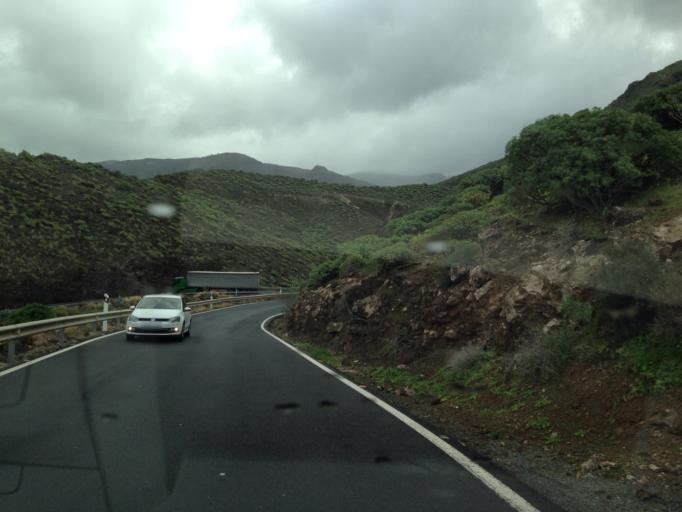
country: ES
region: Canary Islands
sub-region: Provincia de Las Palmas
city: Agaete
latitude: 28.0926
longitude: -15.7011
